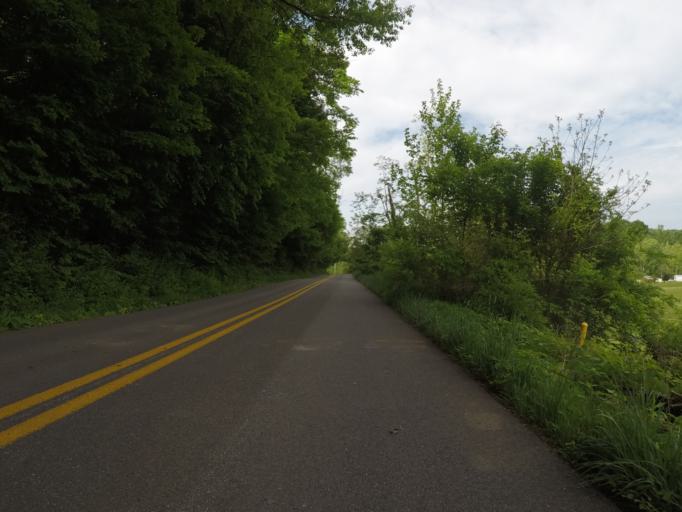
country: US
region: West Virginia
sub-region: Wayne County
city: Ceredo
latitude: 38.3434
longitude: -82.5696
